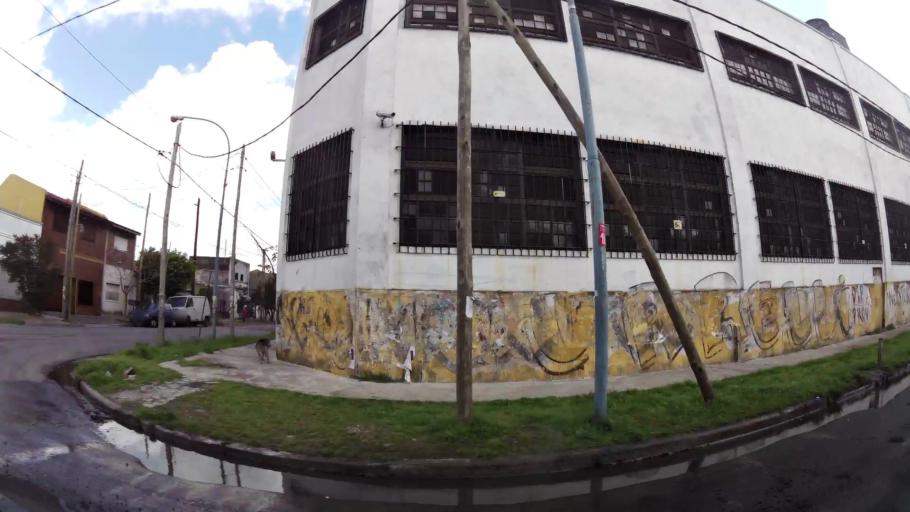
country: AR
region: Buenos Aires
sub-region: Partido de Lanus
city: Lanus
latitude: -34.6790
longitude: -58.4115
